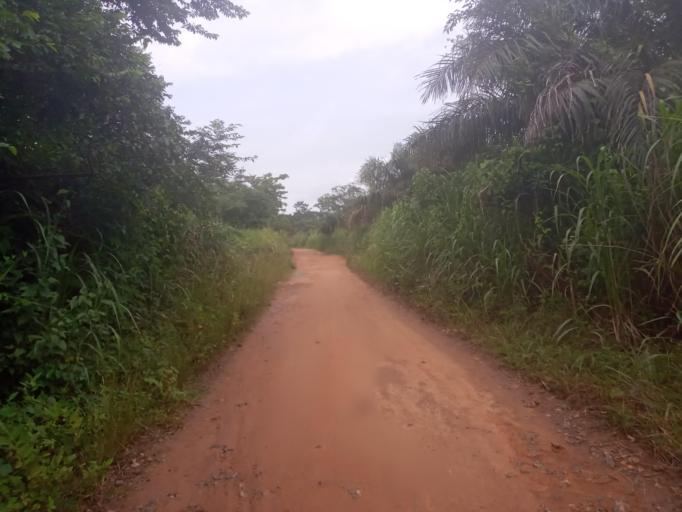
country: SL
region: Northern Province
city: Bumbuna
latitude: 8.9592
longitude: -11.7588
